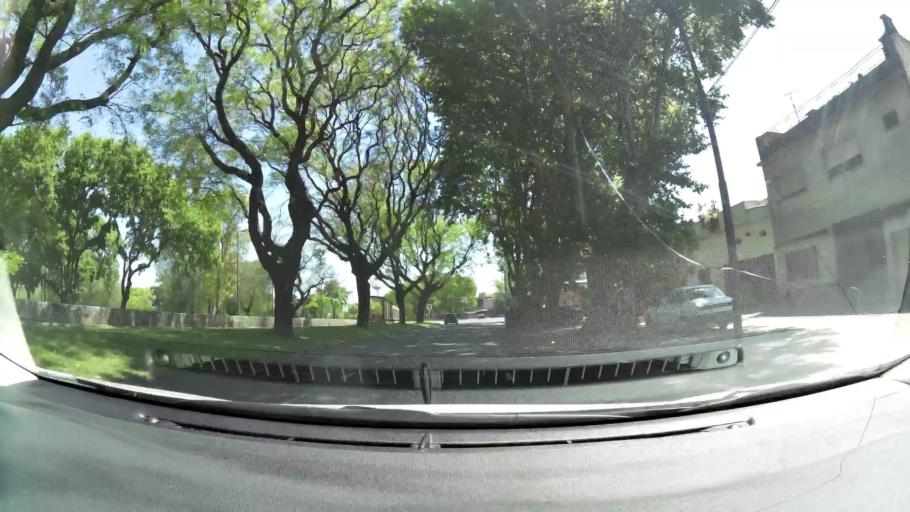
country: AR
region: Buenos Aires F.D.
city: Villa Lugano
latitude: -34.6631
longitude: -58.4366
